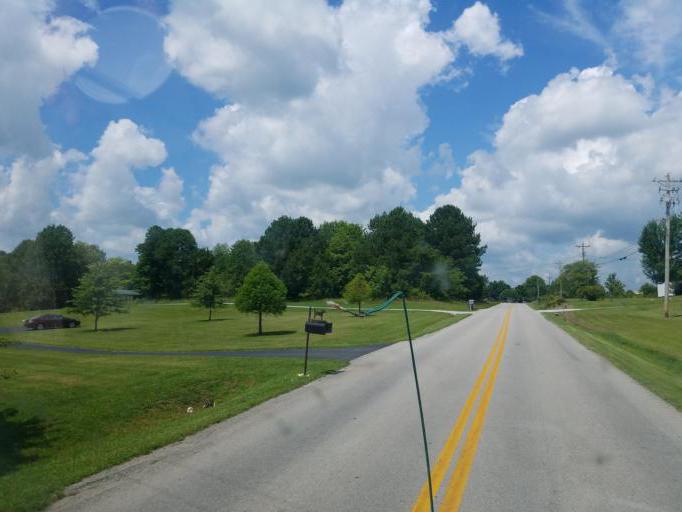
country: US
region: Kentucky
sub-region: Grayson County
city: Leitchfield
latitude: 37.5069
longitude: -86.3188
